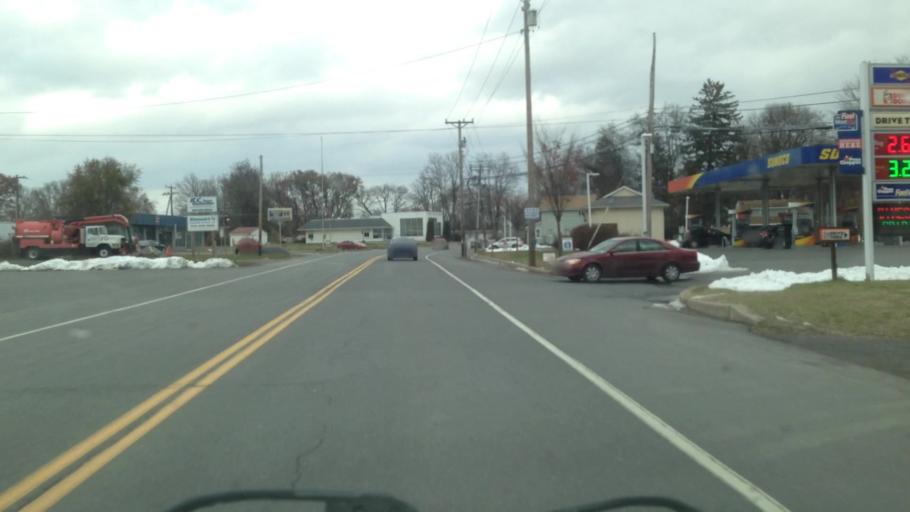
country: US
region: New York
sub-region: Ulster County
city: Saugerties South
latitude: 42.0539
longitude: -73.9564
